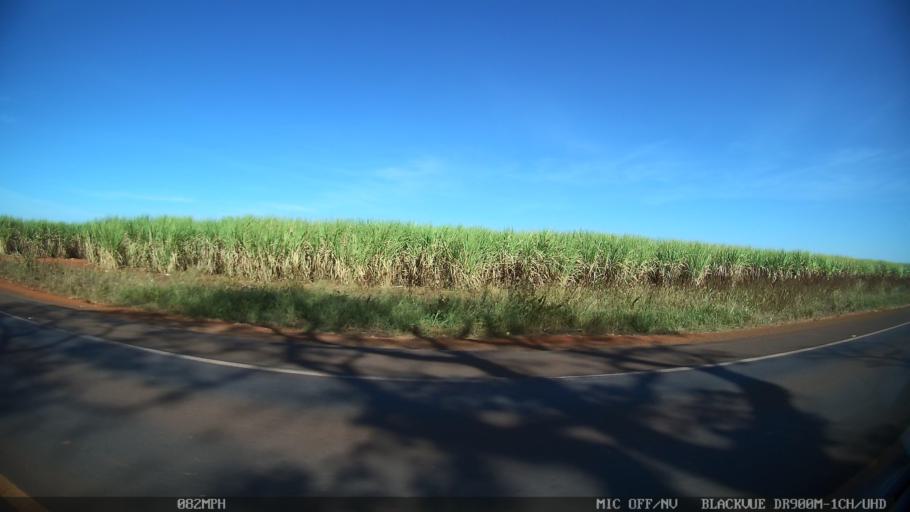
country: BR
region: Sao Paulo
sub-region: Guaira
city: Guaira
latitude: -20.4440
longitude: -48.3518
